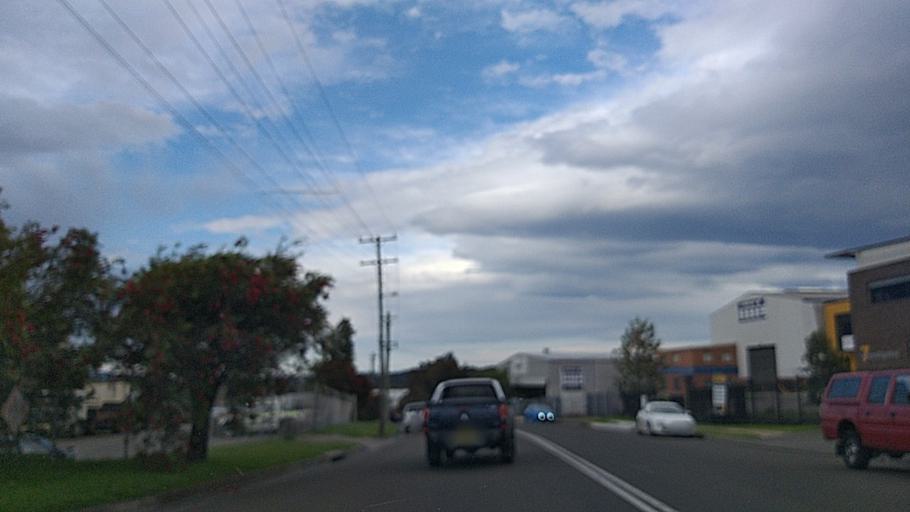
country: AU
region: New South Wales
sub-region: Wollongong
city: Cordeaux Heights
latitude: -34.4583
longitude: 150.8466
